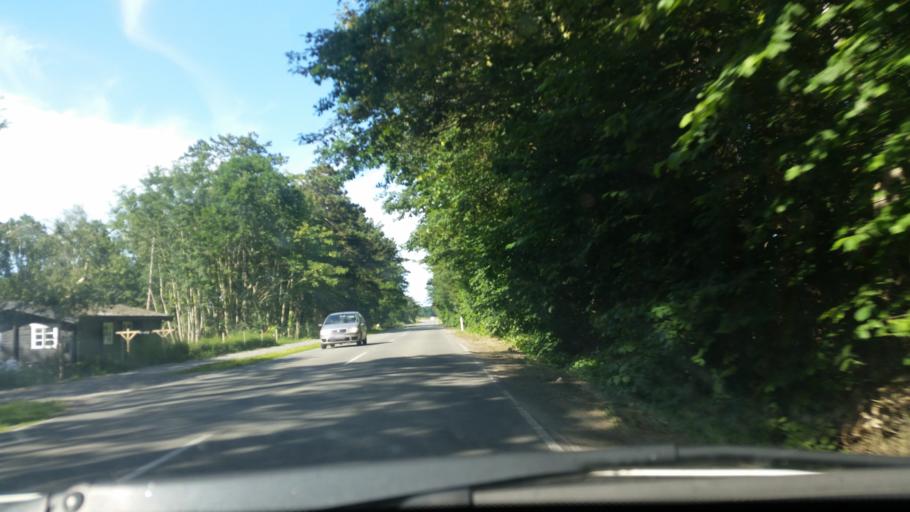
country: DK
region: Central Jutland
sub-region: Samso Kommune
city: Tranebjerg
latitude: 55.8642
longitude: 10.5796
